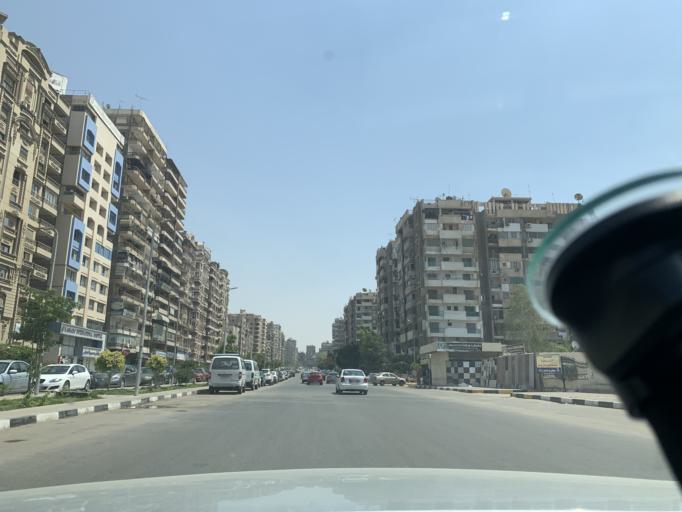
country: EG
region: Muhafazat al Qahirah
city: Cairo
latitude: 30.0689
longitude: 31.3486
